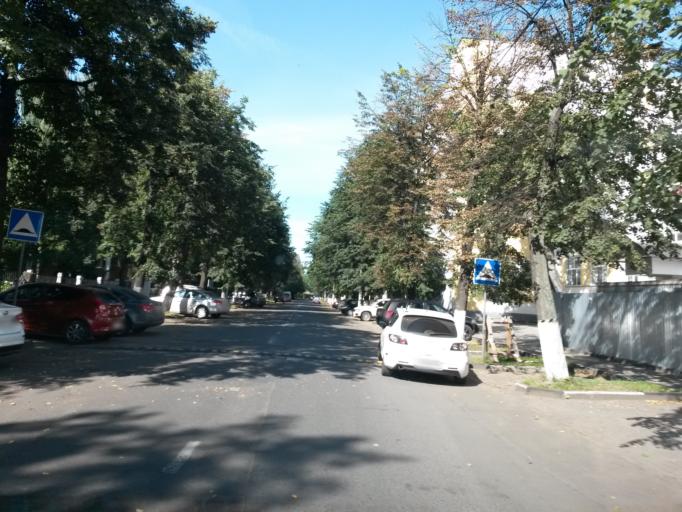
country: RU
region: Jaroslavl
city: Yaroslavl
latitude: 57.6358
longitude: 39.8878
